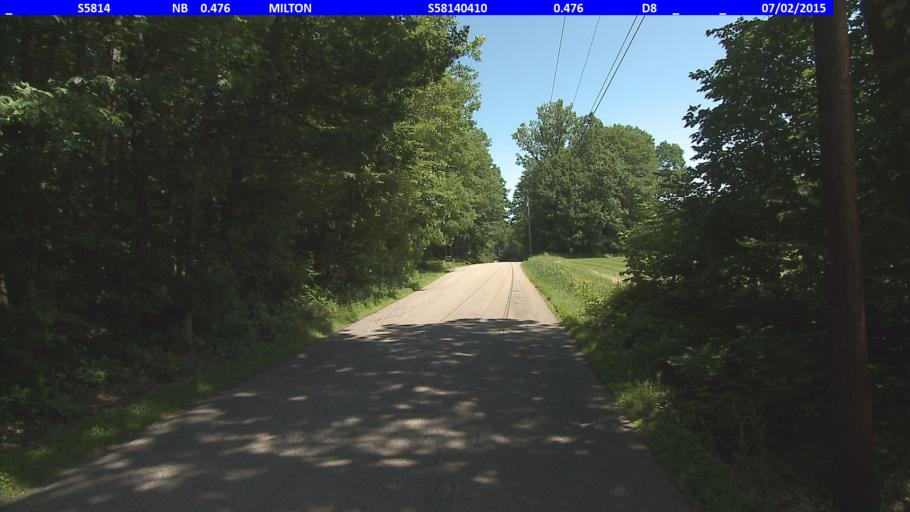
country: US
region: Vermont
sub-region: Chittenden County
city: Milton
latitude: 44.6365
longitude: -73.1743
